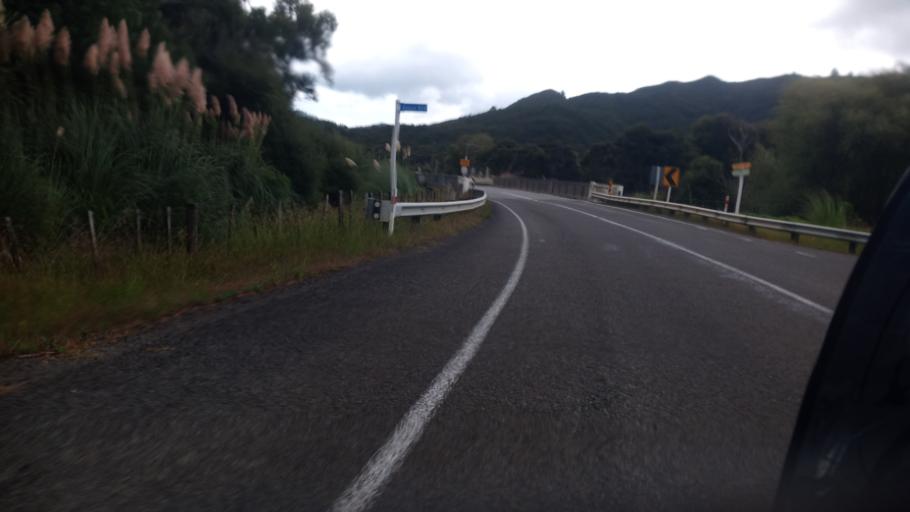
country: NZ
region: Gisborne
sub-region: Gisborne District
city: Gisborne
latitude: -38.2781
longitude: 178.2625
